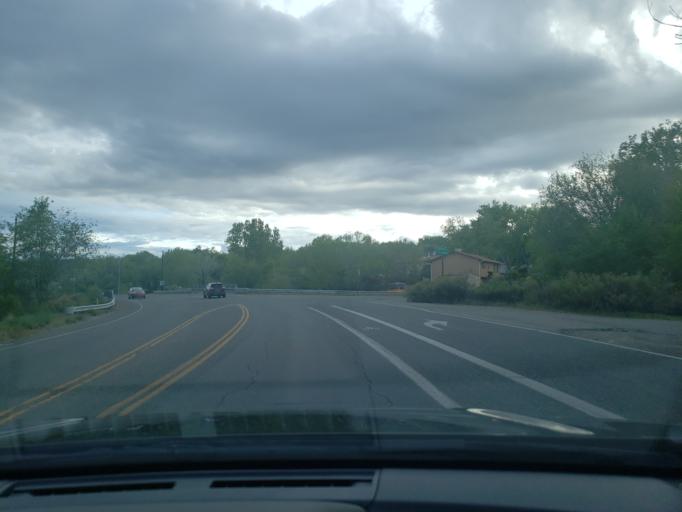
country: US
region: Colorado
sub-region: Mesa County
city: Grand Junction
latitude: 39.0631
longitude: -108.5874
